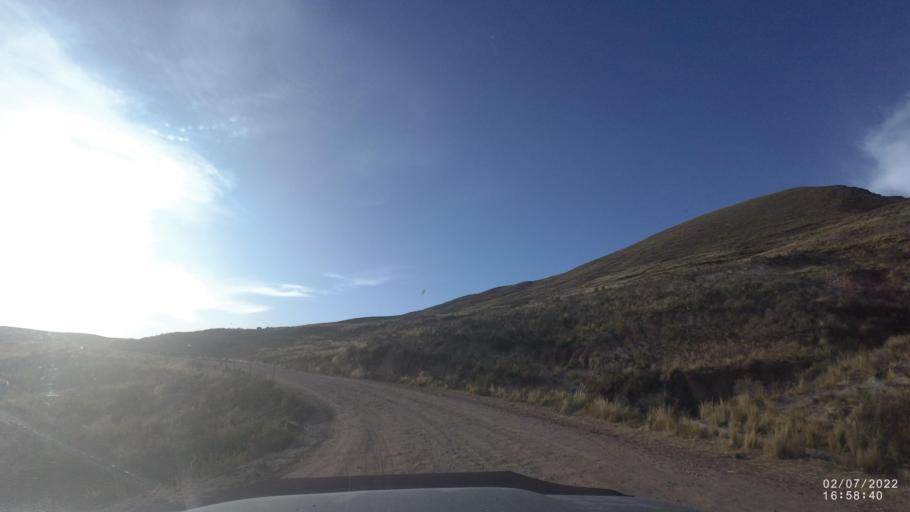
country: BO
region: Cochabamba
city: Irpa Irpa
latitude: -17.9446
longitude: -66.5474
